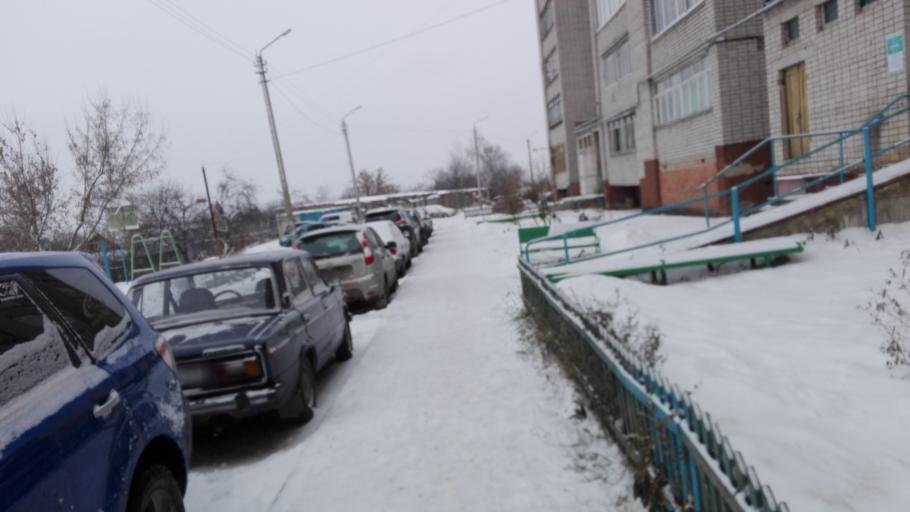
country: RU
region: Tula
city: Kosaya Gora
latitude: 54.1223
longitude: 37.5391
